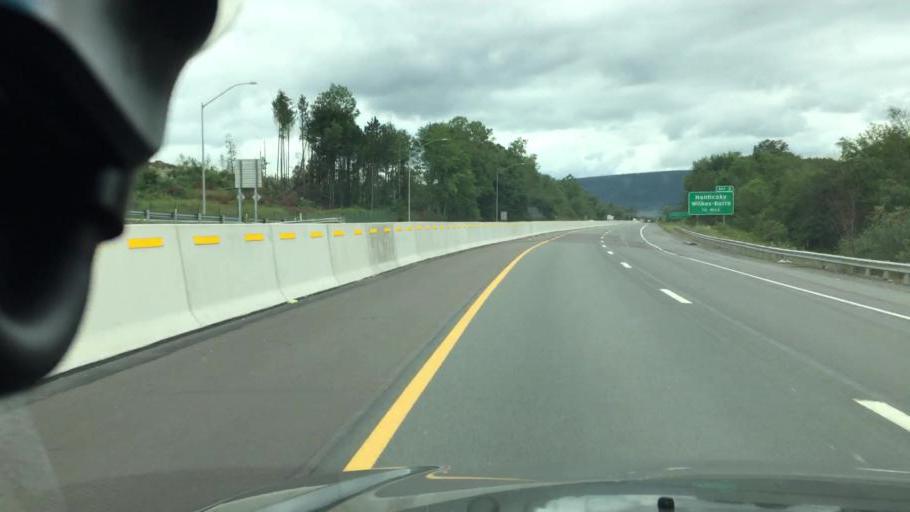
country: US
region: Pennsylvania
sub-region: Luzerne County
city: Nanticoke
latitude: 41.2002
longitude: -75.9671
